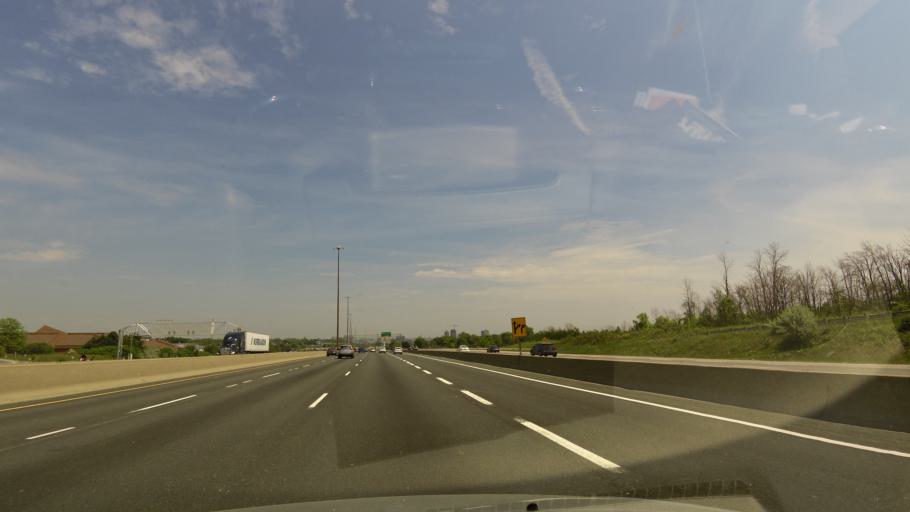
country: CA
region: Ontario
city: Pickering
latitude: 43.8169
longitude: -79.1140
